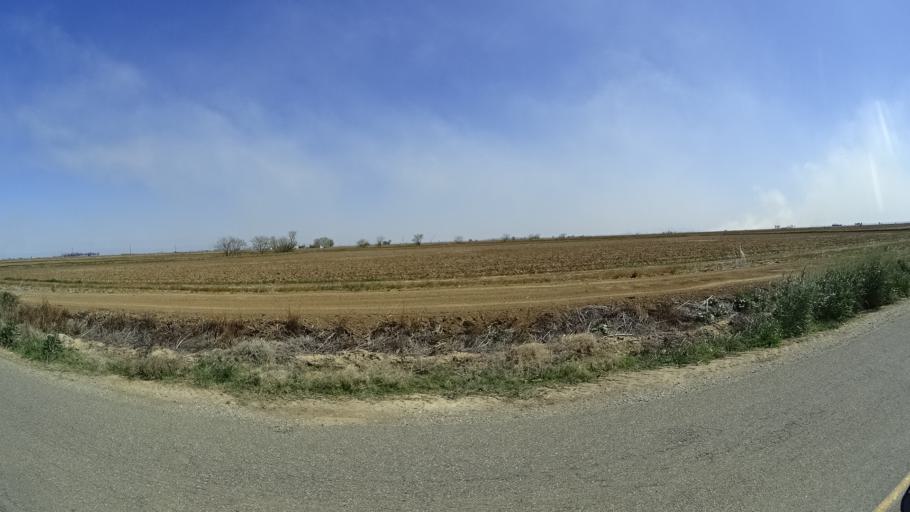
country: US
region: California
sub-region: Glenn County
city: Willows
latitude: 39.4047
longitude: -122.2484
